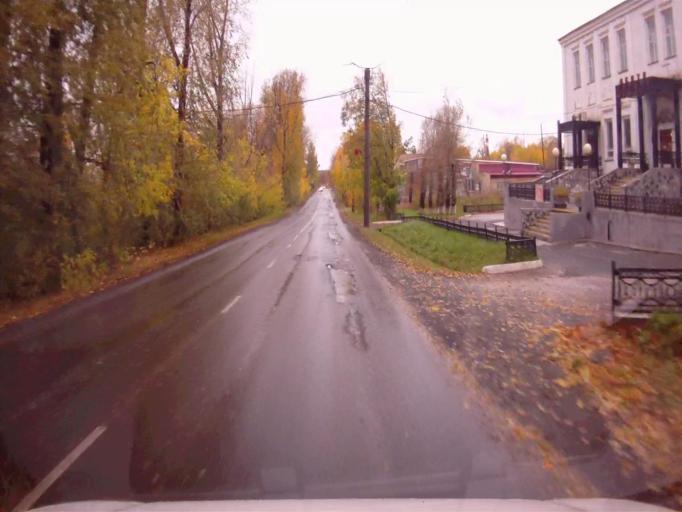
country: RU
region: Chelyabinsk
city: Verkhniy Ufaley
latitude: 56.0388
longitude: 60.2548
